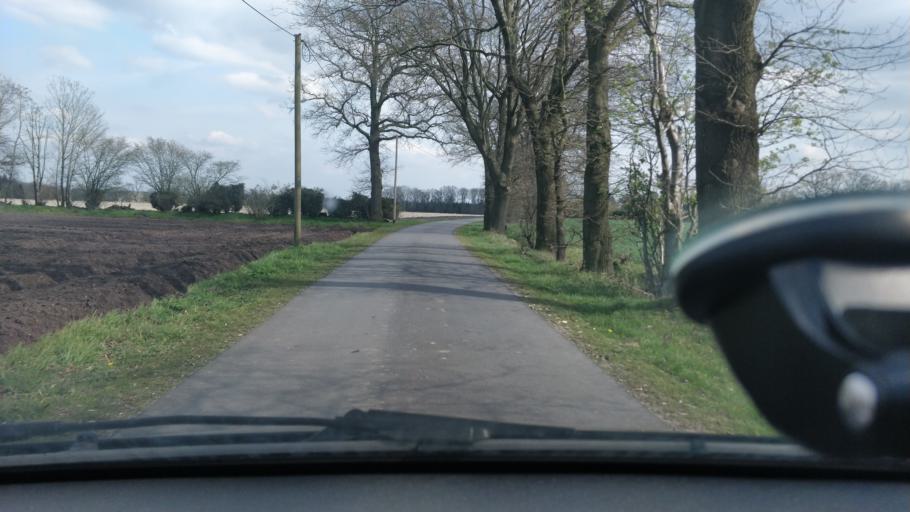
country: DE
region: North Rhine-Westphalia
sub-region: Regierungsbezirk Dusseldorf
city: Bocholt
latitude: 51.8893
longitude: 6.6309
